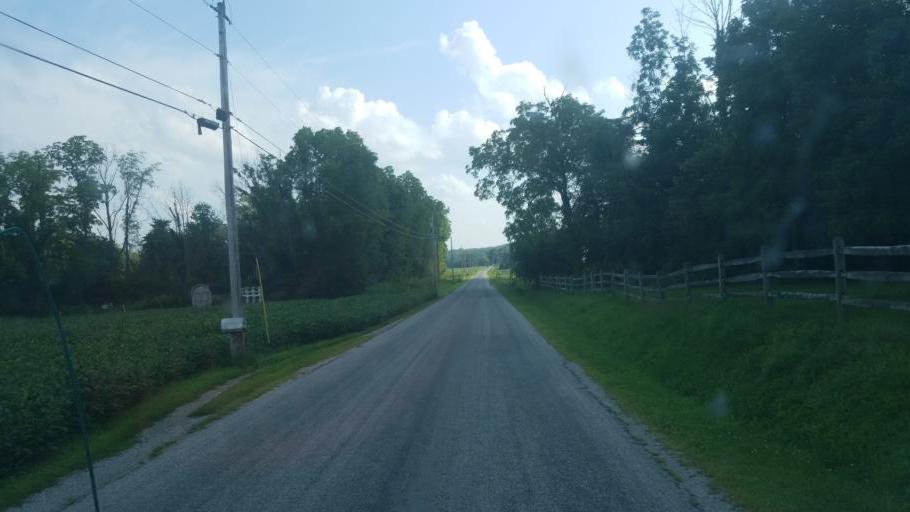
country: US
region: Ohio
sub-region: Medina County
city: Lodi
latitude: 40.9655
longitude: -82.0350
